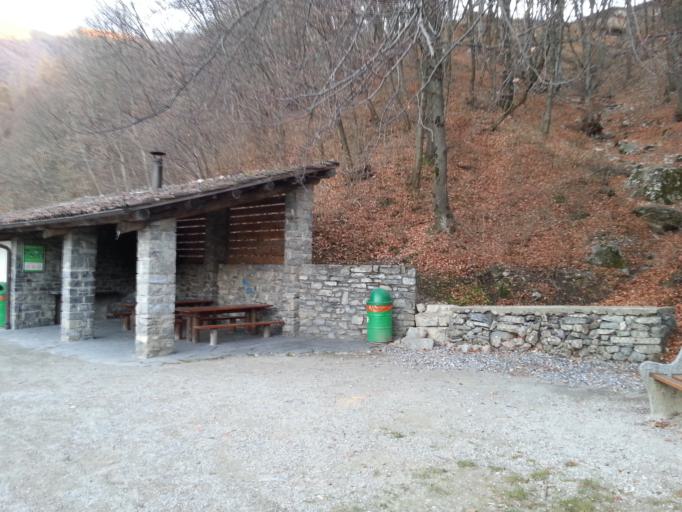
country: CH
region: Ticino
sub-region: Lugano District
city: Pregassona
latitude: 46.0143
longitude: 8.9991
